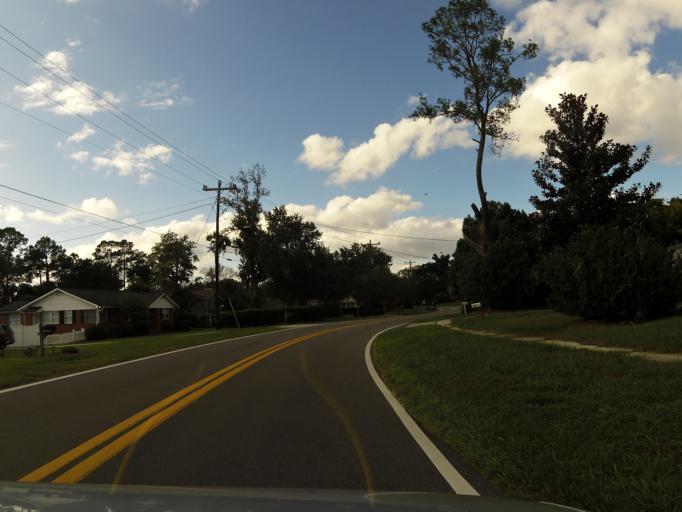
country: US
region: Florida
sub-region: Clay County
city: Bellair-Meadowbrook Terrace
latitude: 30.2694
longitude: -81.7280
